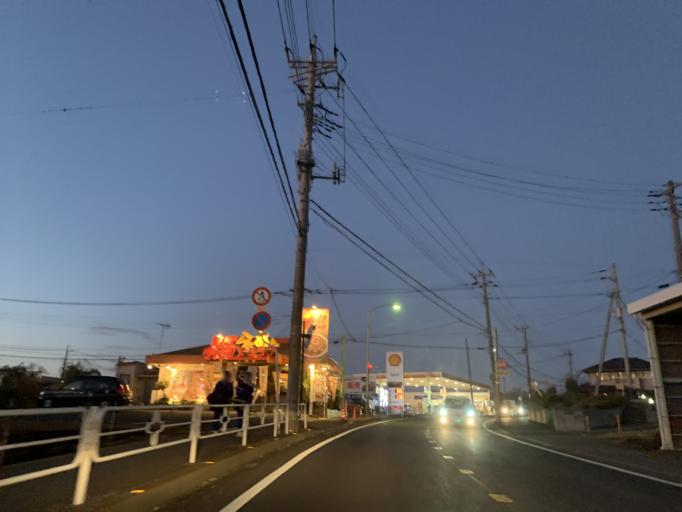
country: JP
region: Chiba
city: Nagareyama
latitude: 35.8937
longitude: 139.9004
